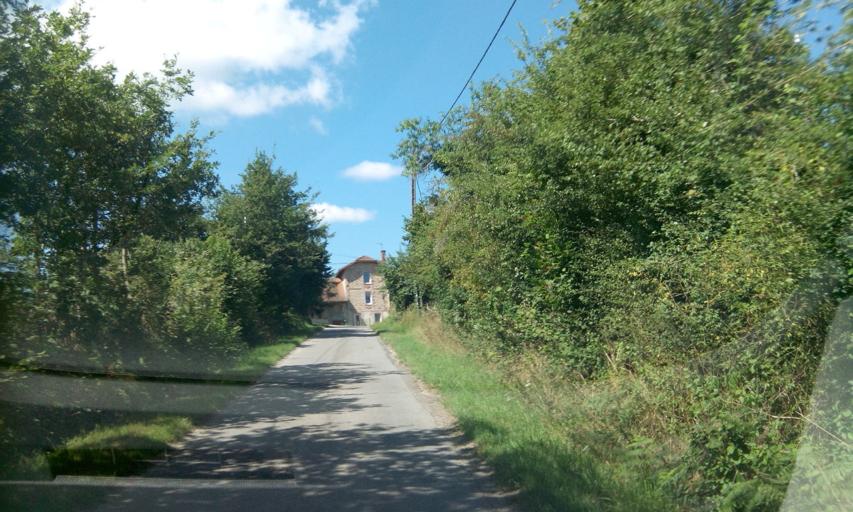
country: FR
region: Limousin
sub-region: Departement de la Haute-Vienne
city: Saint-Leonard-de-Noblat
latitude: 45.8080
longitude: 1.4897
